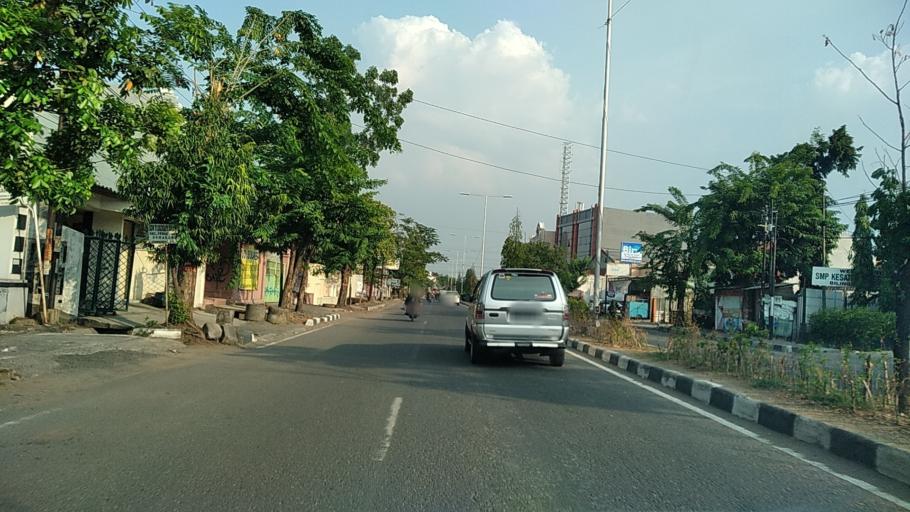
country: ID
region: Central Java
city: Semarang
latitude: -6.9975
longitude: 110.4636
